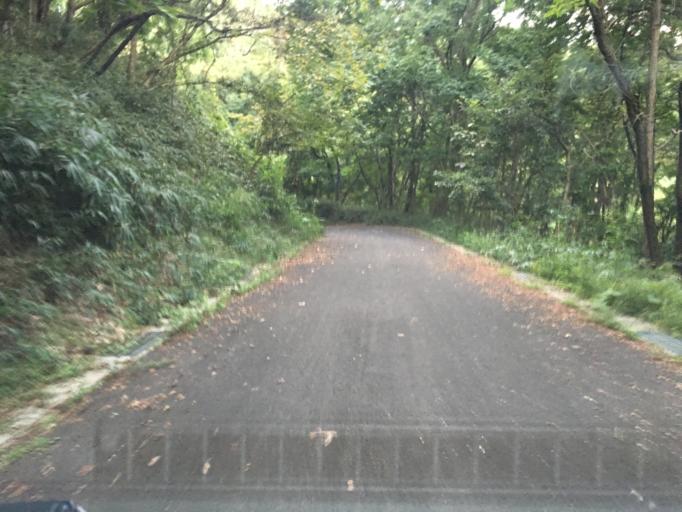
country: JP
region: Fukushima
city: Fukushima-shi
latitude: 37.7528
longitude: 140.5028
